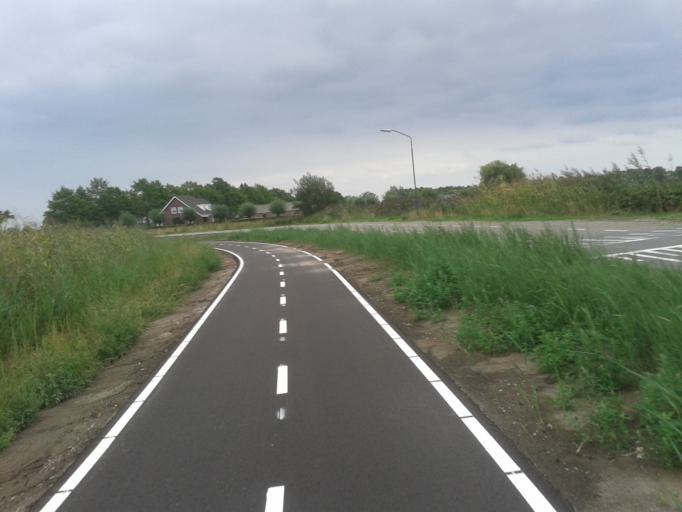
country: NL
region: North Brabant
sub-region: Gemeente Hilvarenbeek
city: Hilvarenbeek
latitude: 51.5182
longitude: 5.1876
